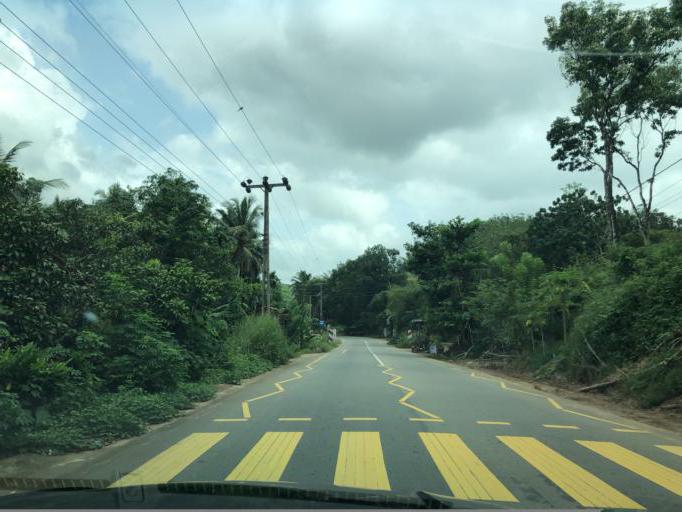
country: LK
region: Western
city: Horana South
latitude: 6.6878
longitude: 80.1382
